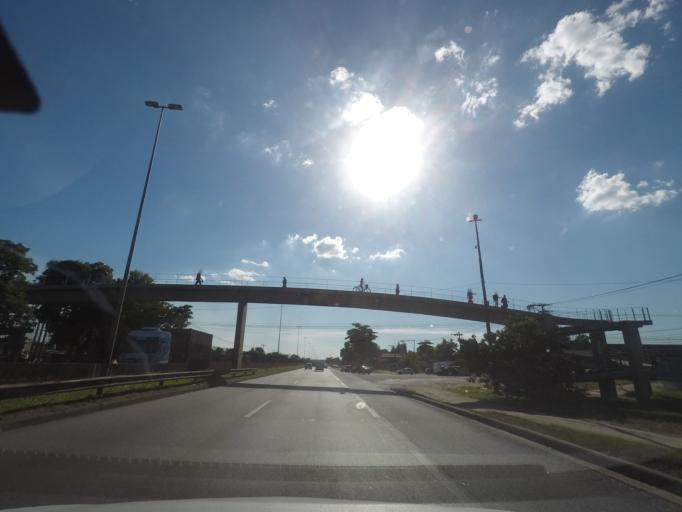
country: BR
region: Rio de Janeiro
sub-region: Petropolis
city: Petropolis
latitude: -22.6488
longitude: -43.2307
